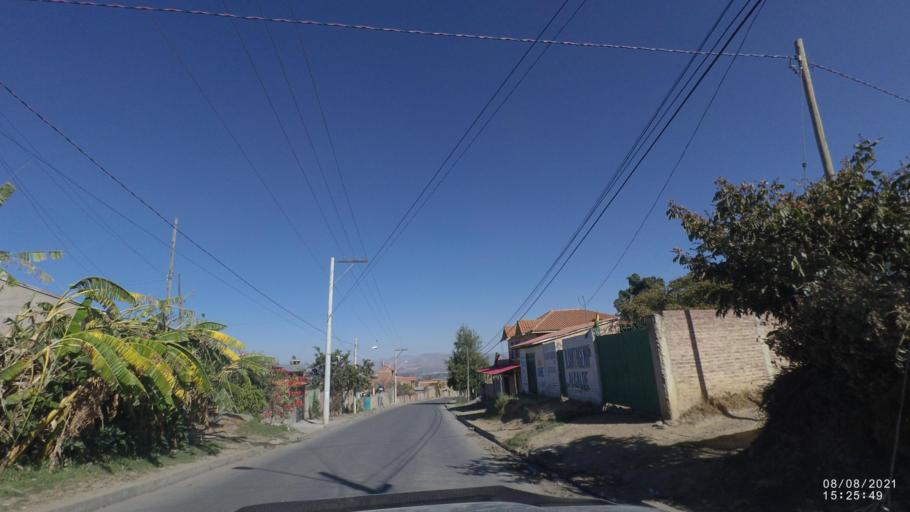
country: BO
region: Cochabamba
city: Cochabamba
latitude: -17.3182
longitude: -66.2821
